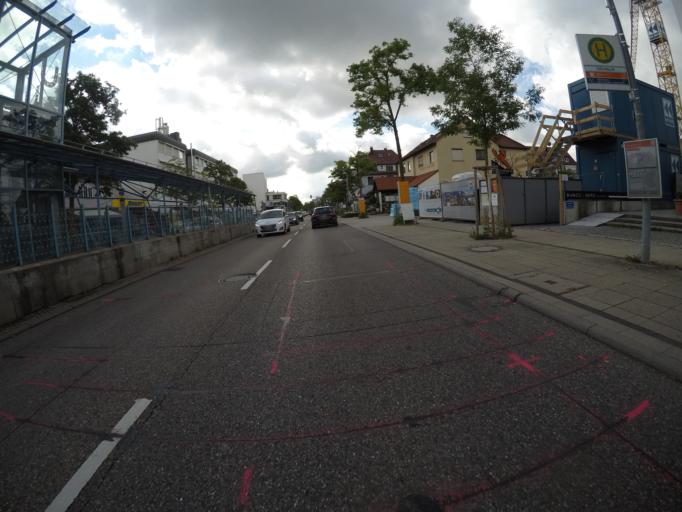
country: DE
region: Baden-Wuerttemberg
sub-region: Regierungsbezirk Stuttgart
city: Stuttgart-Ost
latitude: 48.7445
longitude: 9.2130
